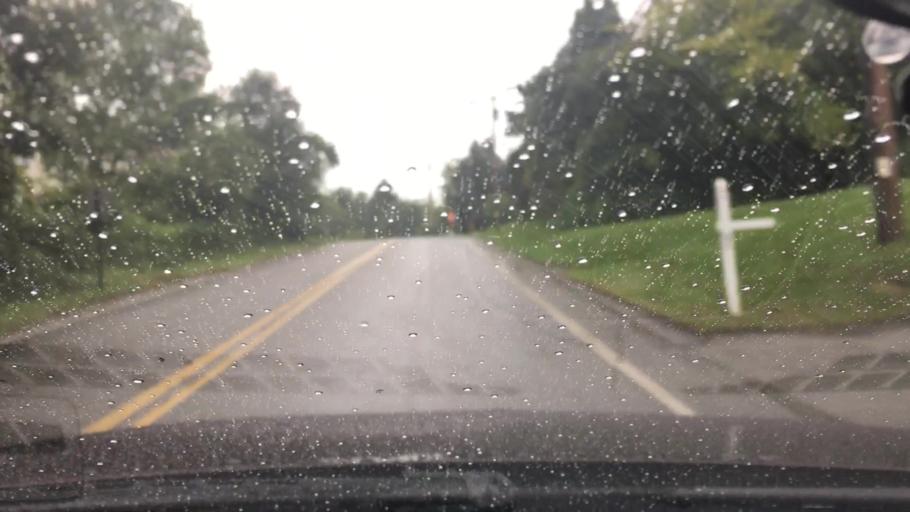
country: US
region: New York
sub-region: Dutchess County
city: Myers Corner
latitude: 41.5932
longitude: -73.8719
